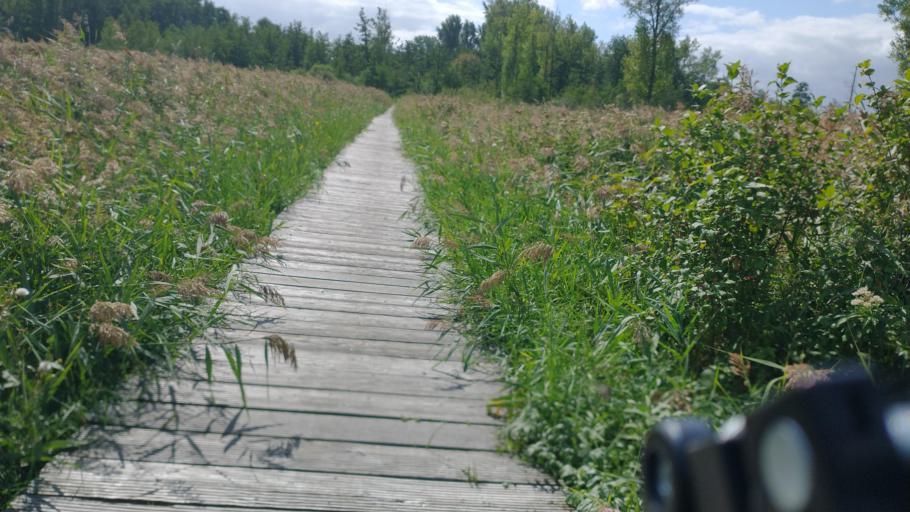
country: DE
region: Schleswig-Holstein
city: Bad Oldesloe
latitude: 53.8185
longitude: 10.3530
